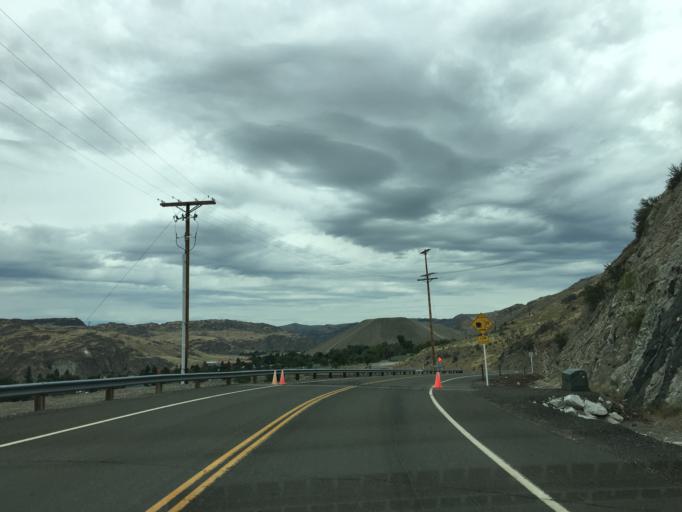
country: US
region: Washington
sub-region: Okanogan County
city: Coulee Dam
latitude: 47.9612
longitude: -118.9717
